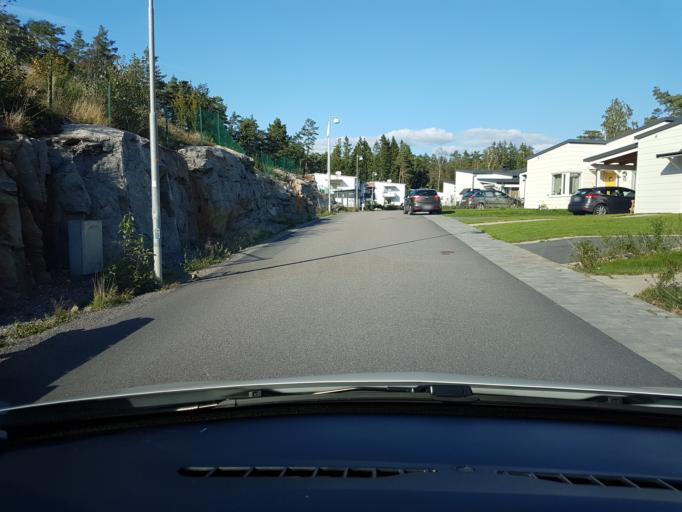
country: SE
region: Vaestra Goetaland
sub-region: Ale Kommun
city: Alafors
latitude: 57.9289
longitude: 12.0967
